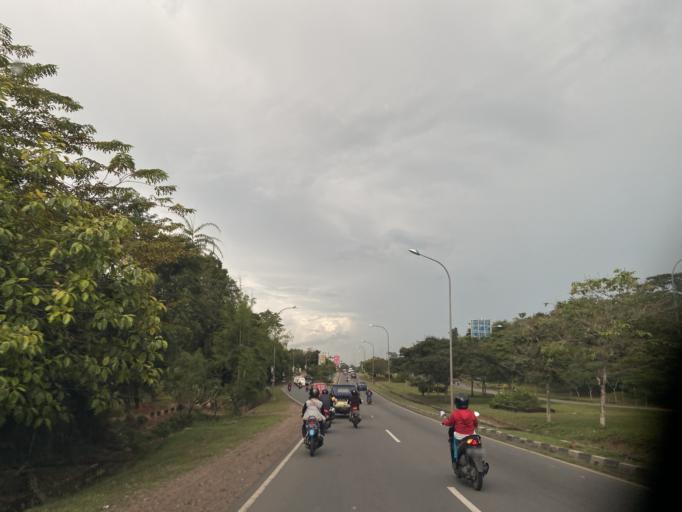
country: SG
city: Singapore
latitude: 1.1000
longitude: 104.0734
